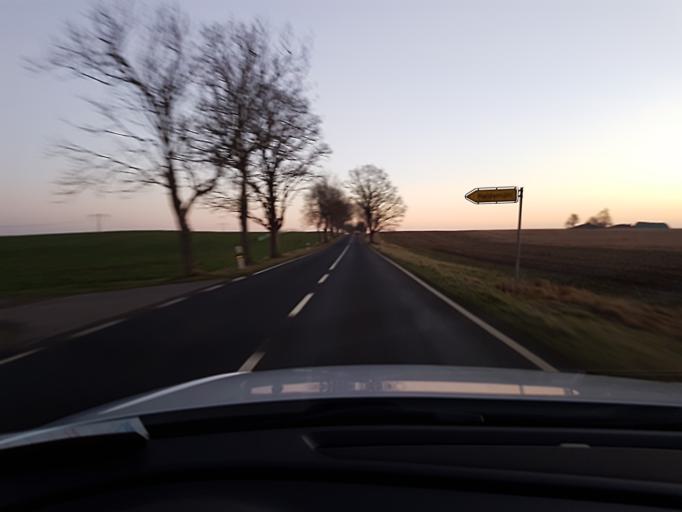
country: DE
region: Mecklenburg-Vorpommern
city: Gingst
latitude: 54.5004
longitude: 13.2796
